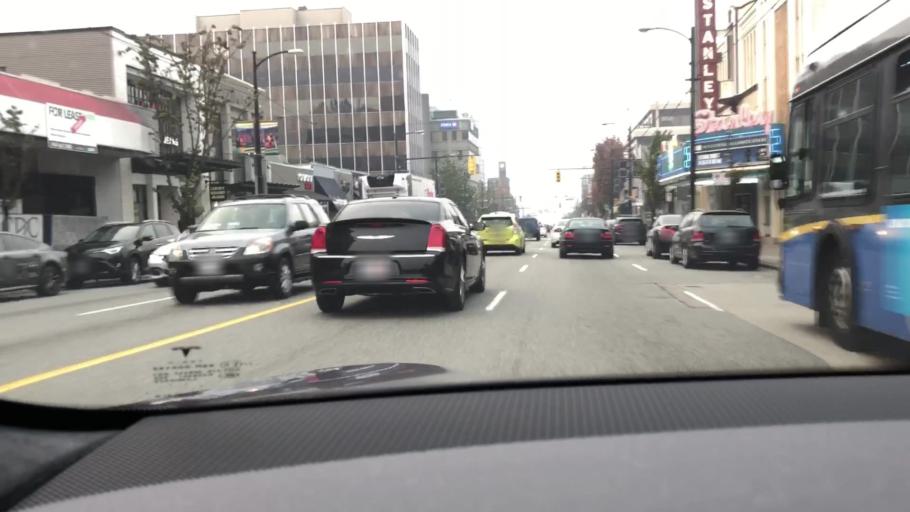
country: CA
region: British Columbia
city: Vancouver
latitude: 49.2610
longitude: -123.1386
